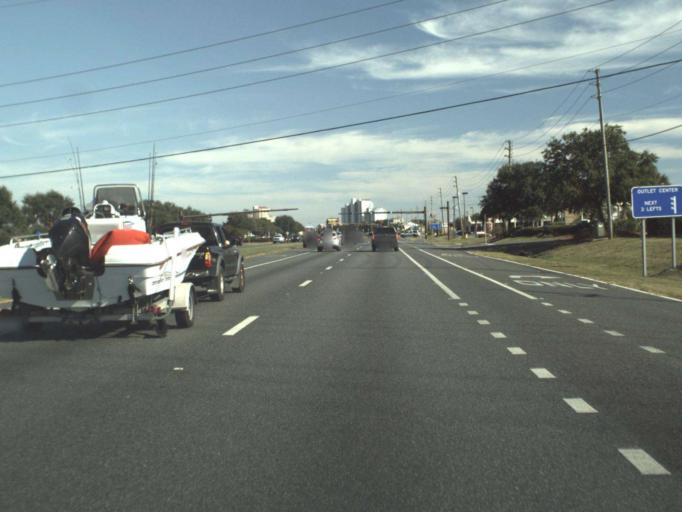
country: US
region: Florida
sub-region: Walton County
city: Miramar Beach
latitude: 30.3795
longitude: -86.3544
